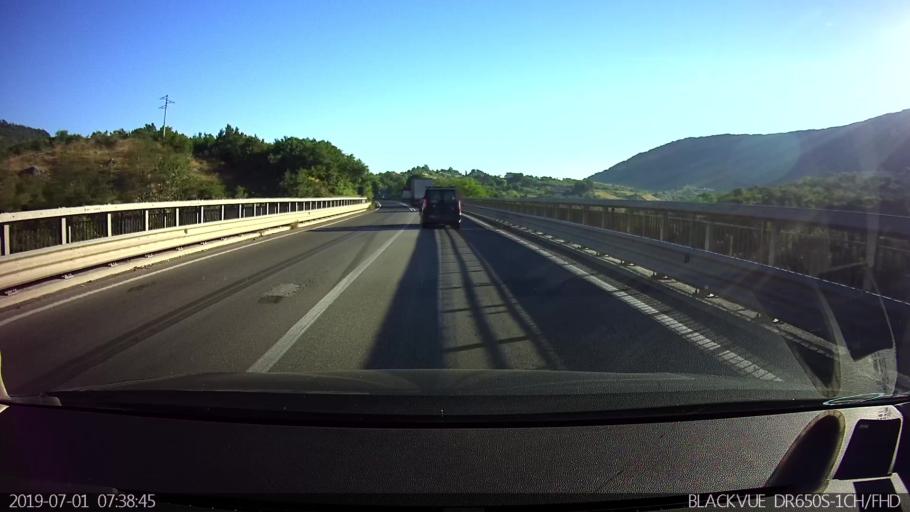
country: IT
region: Latium
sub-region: Provincia di Frosinone
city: Giuliano di Roma
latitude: 41.5450
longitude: 13.2694
